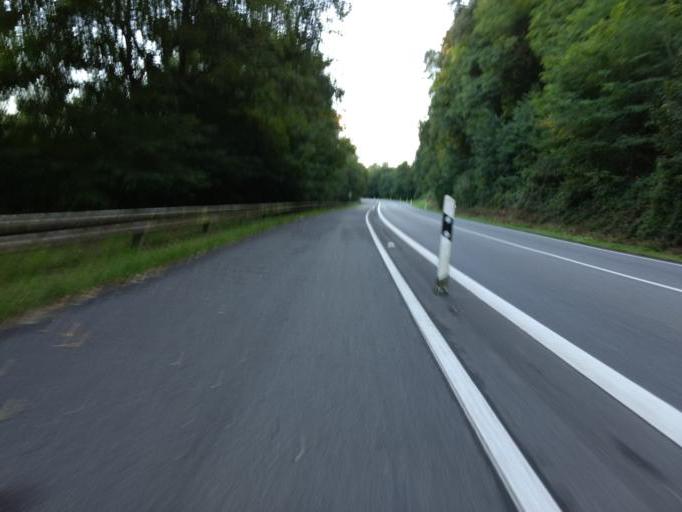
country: DE
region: Saarland
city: Rehlingen-Siersburg
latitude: 49.3887
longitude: 6.6653
